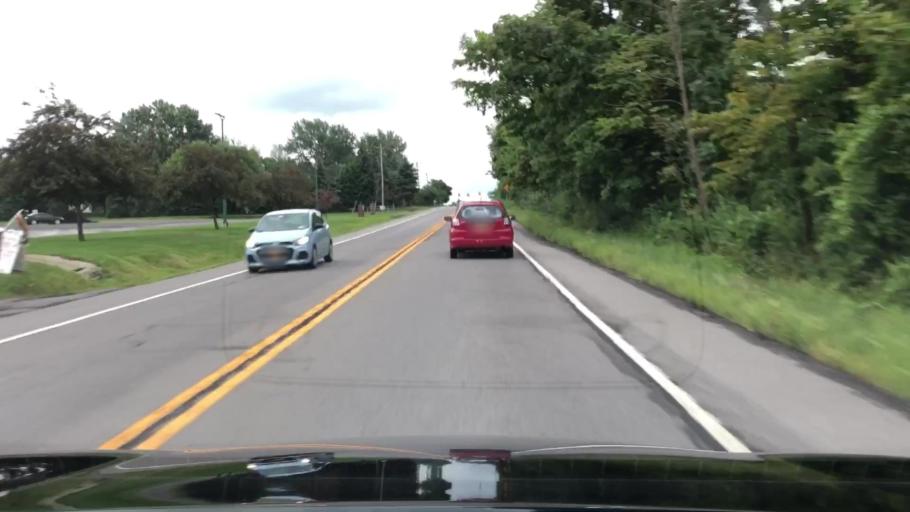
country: US
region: New York
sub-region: Erie County
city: Orchard Park
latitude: 42.7716
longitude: -78.6968
